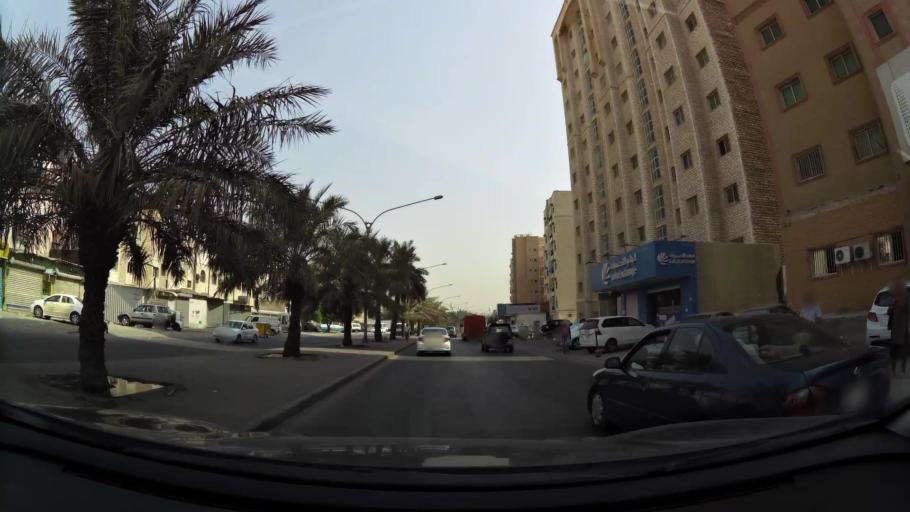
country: KW
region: Al Farwaniyah
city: Al Farwaniyah
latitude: 29.2592
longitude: 47.9314
